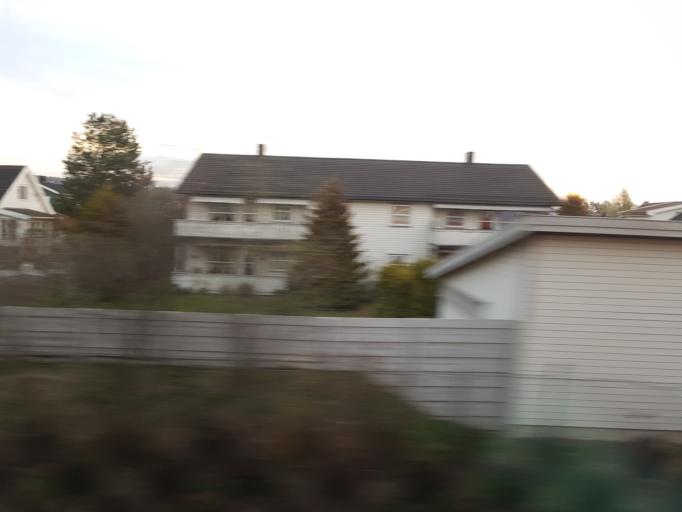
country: NO
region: Hedmark
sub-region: Hamar
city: Hamar
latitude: 60.7990
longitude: 11.0423
